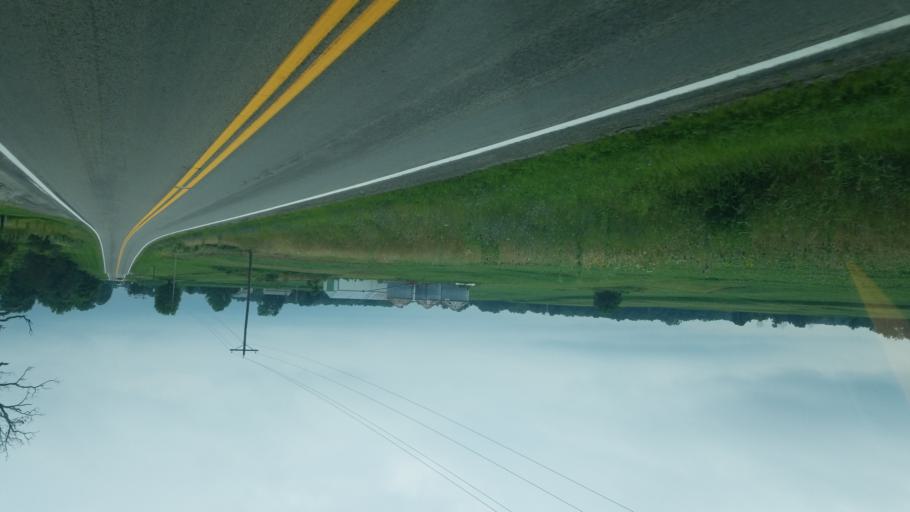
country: US
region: Ohio
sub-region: Logan County
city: Northwood
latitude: 40.5882
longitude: -83.8019
